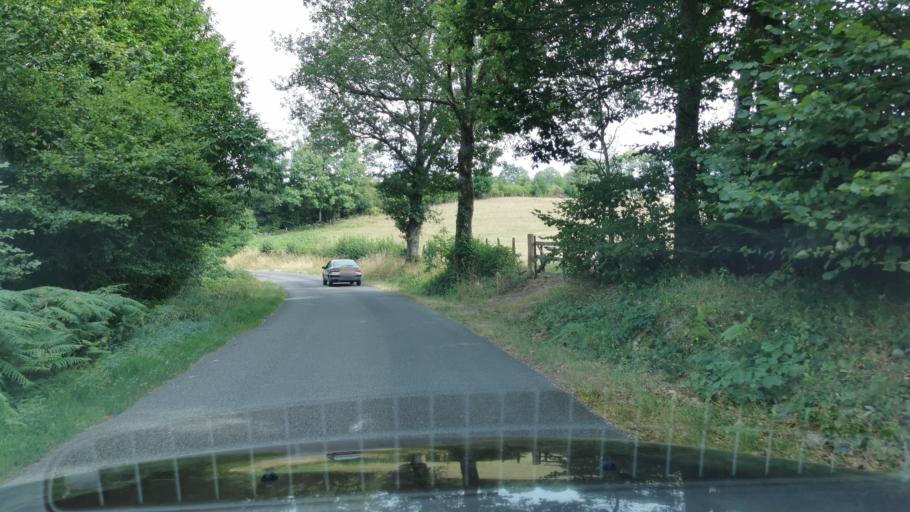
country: FR
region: Bourgogne
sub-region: Departement de Saone-et-Loire
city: Marmagne
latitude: 46.8061
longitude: 4.2930
